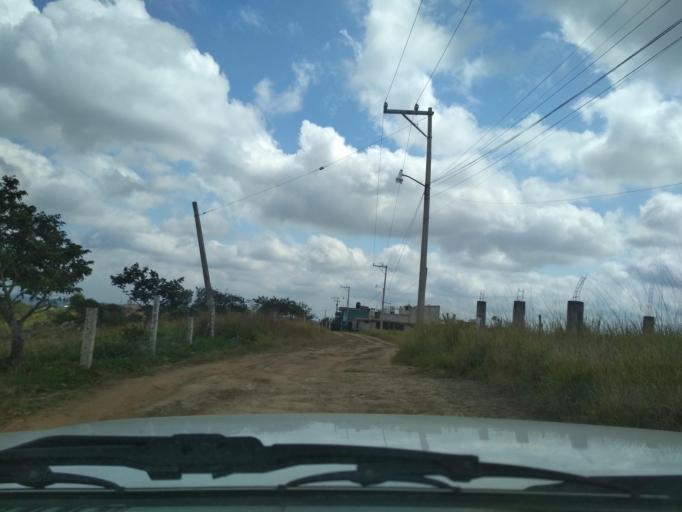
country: MX
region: Veracruz
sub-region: Emiliano Zapata
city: Jacarandas
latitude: 19.4968
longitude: -96.8408
